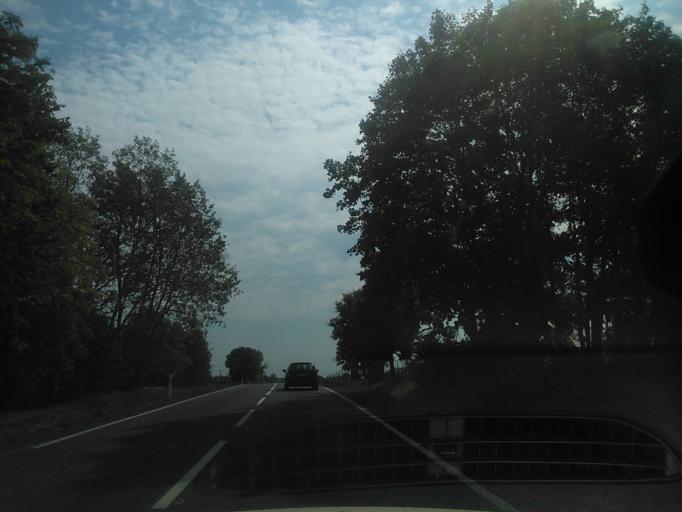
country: PL
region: Warmian-Masurian Voivodeship
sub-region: Powiat dzialdowski
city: Lidzbark
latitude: 53.2408
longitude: 19.9289
